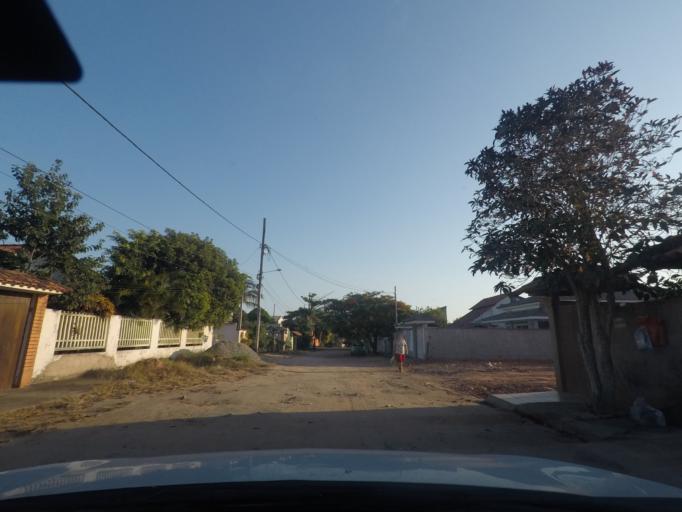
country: BR
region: Rio de Janeiro
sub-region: Marica
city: Marica
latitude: -22.9687
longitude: -42.9280
